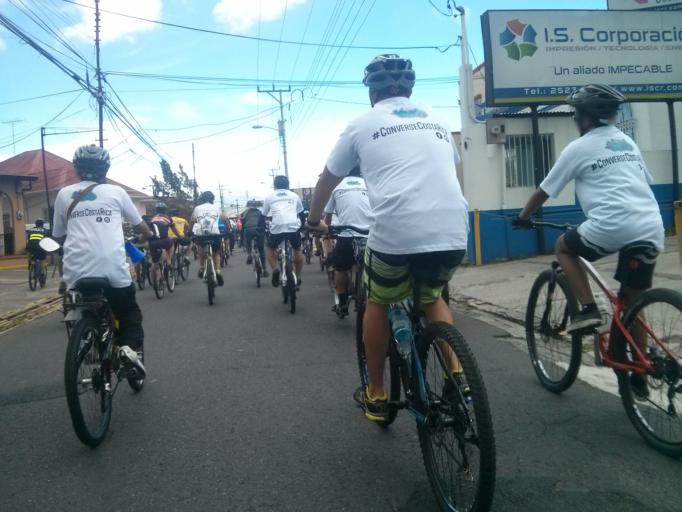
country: CR
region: San Jose
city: San Jose
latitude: 9.9303
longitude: -84.0675
